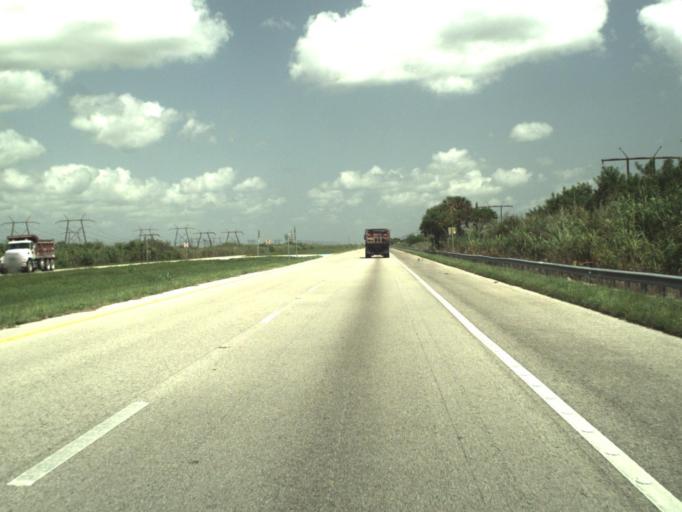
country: US
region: Florida
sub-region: Broward County
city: Weston
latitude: 26.2858
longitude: -80.4998
